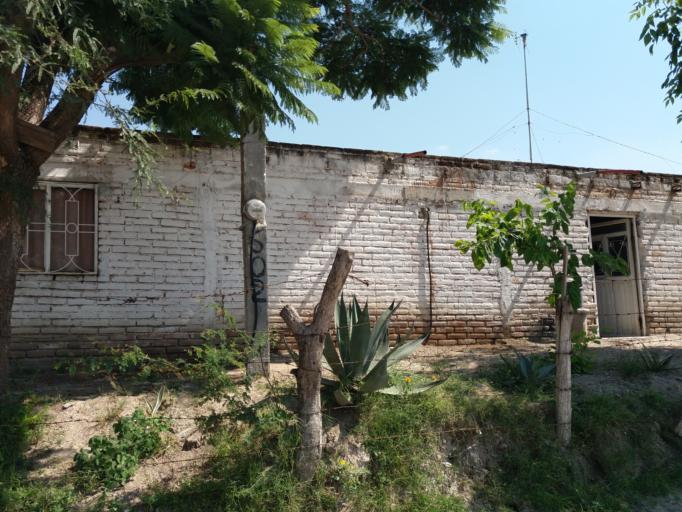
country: MX
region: Aguascalientes
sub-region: Aguascalientes
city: Penuelas (El Cienegal)
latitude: 21.7505
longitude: -102.3032
